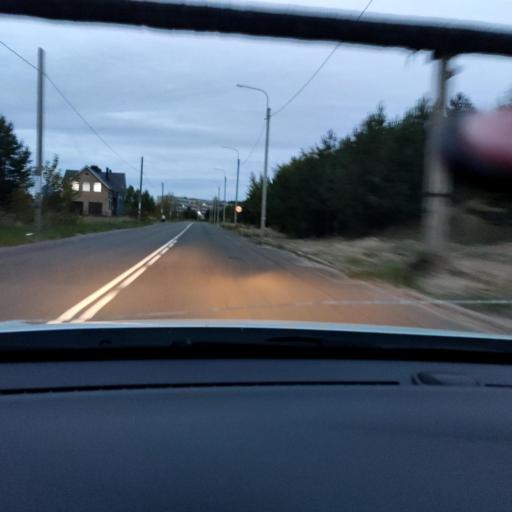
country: RU
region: Mariy-El
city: Volzhsk
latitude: 55.8745
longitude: 48.3810
